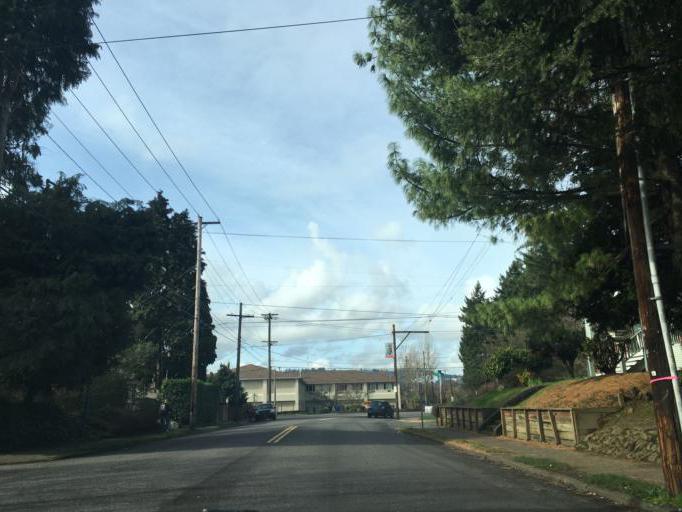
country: US
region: Oregon
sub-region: Clackamas County
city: Milwaukie
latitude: 45.4904
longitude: -122.6292
